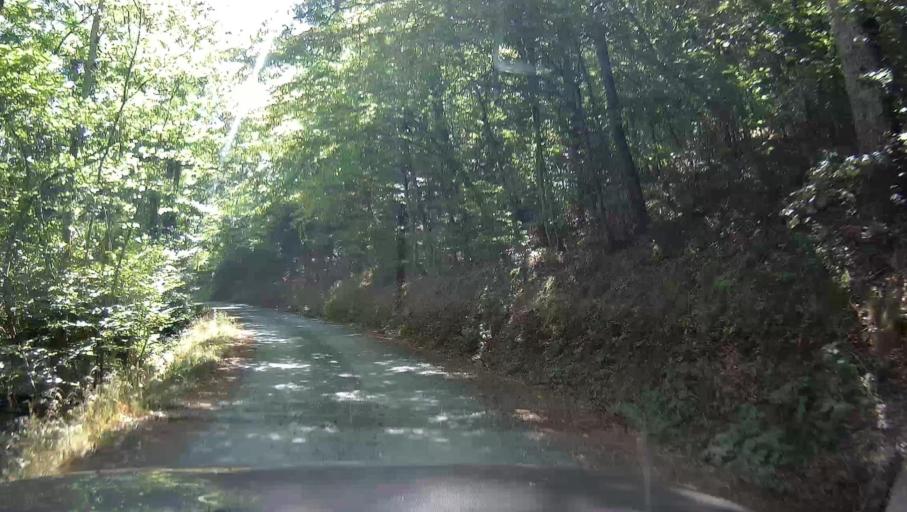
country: FR
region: Rhone-Alpes
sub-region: Departement du Rhone
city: Grandris
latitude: 46.0108
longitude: 4.5379
